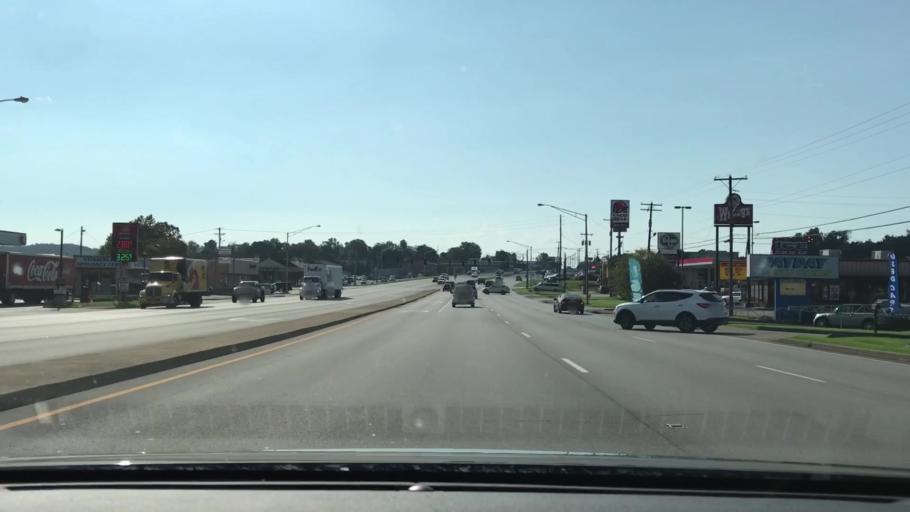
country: US
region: Kentucky
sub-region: Pulaski County
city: Somerset
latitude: 37.0926
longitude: -84.6183
